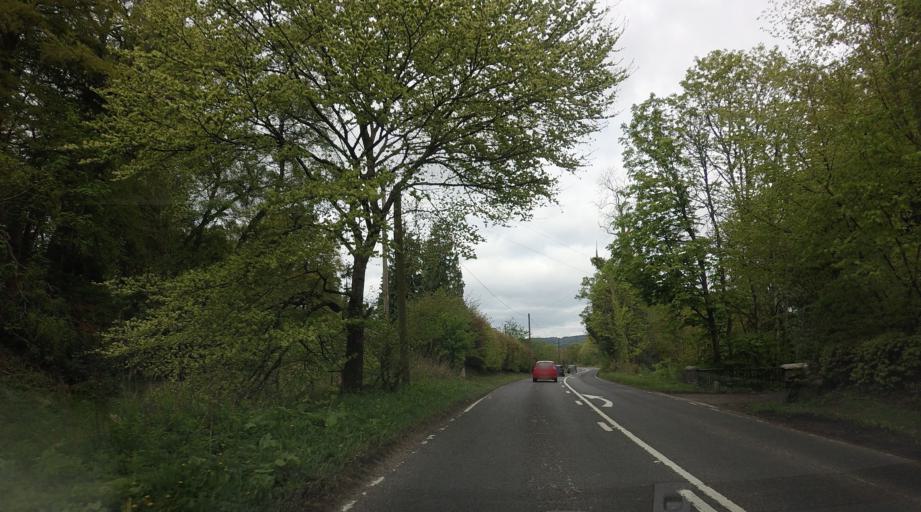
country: GB
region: Scotland
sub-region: Perth and Kinross
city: Abernethy
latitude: 56.3228
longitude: -3.3541
